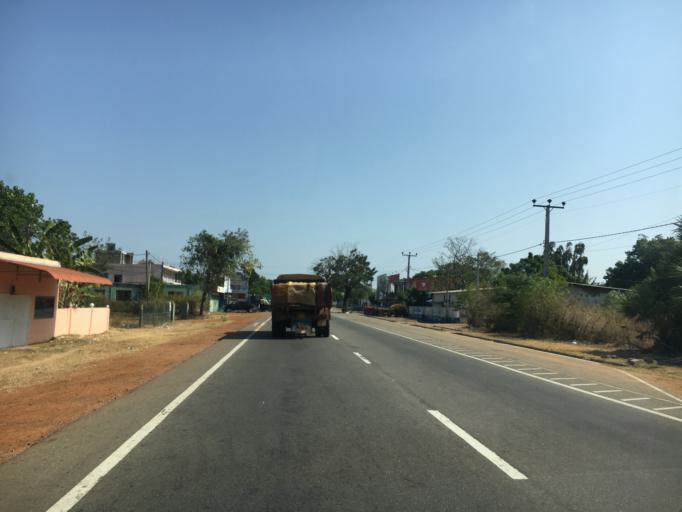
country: LK
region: Northern Province
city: Kilinochchi
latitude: 9.4335
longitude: 80.4077
